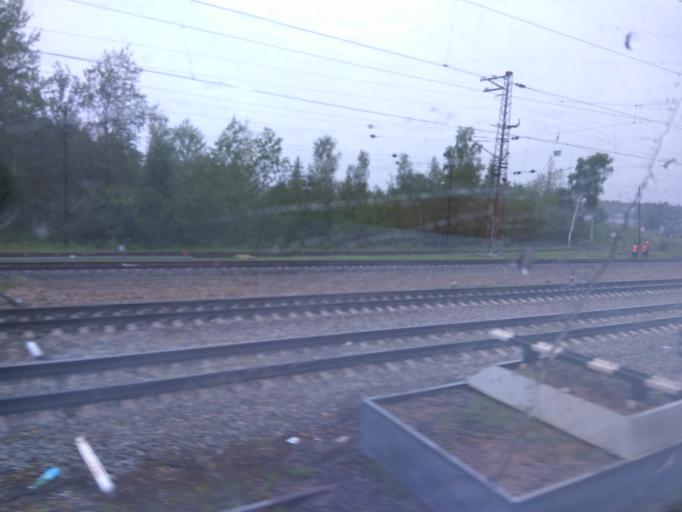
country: RU
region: Moskovskaya
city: Zhilevo
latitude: 54.9906
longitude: 38.0291
